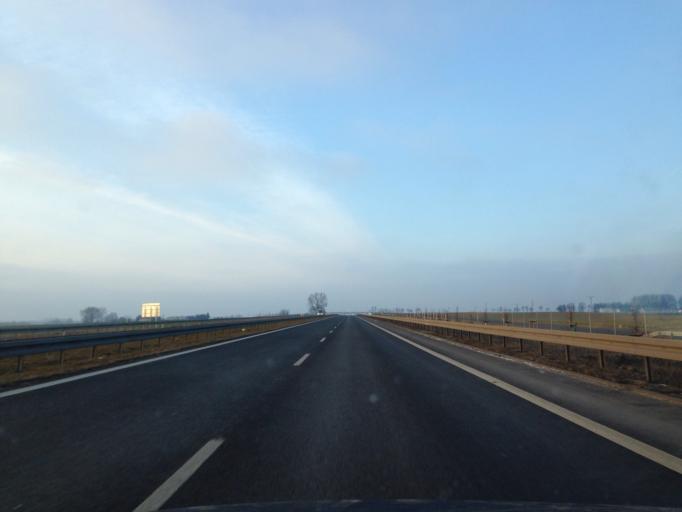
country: PL
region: Greater Poland Voivodeship
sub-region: Powiat gnieznienski
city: Gniezno
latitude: 52.5299
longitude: 17.5409
